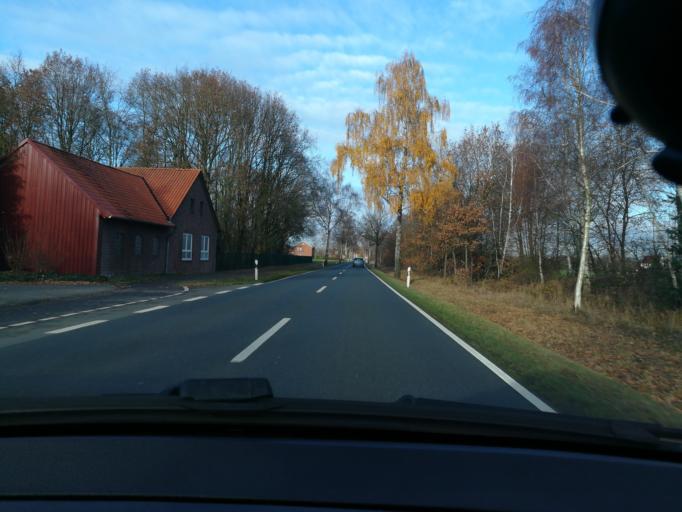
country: DE
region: Lower Saxony
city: Schwaforden
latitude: 52.7271
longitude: 8.8158
